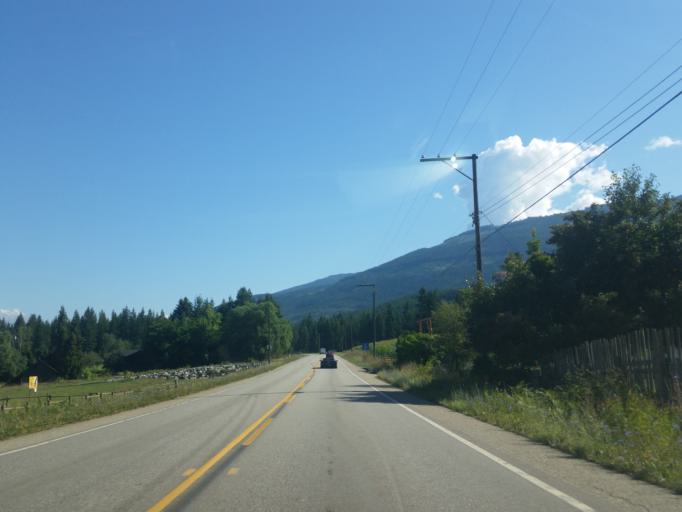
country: CA
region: British Columbia
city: Enderby
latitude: 50.6729
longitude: -119.0596
